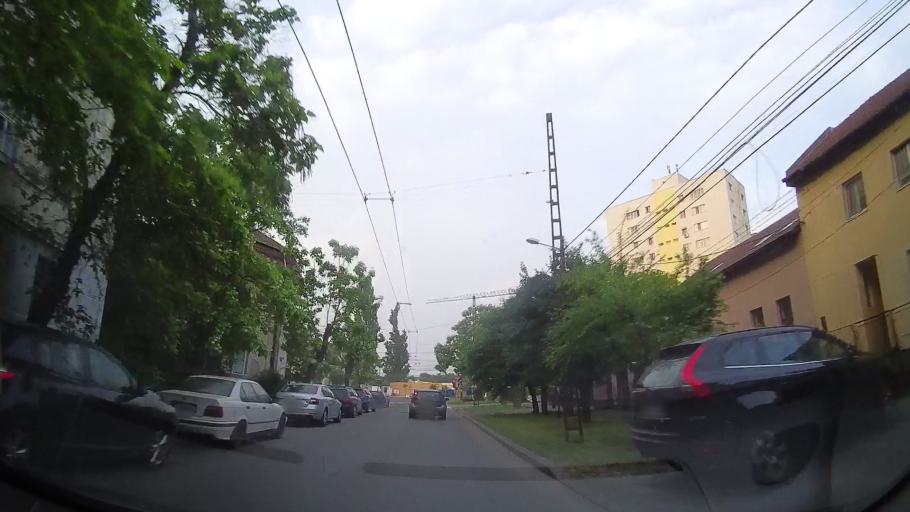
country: RO
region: Timis
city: Timisoara
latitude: 45.7622
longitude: 21.2437
